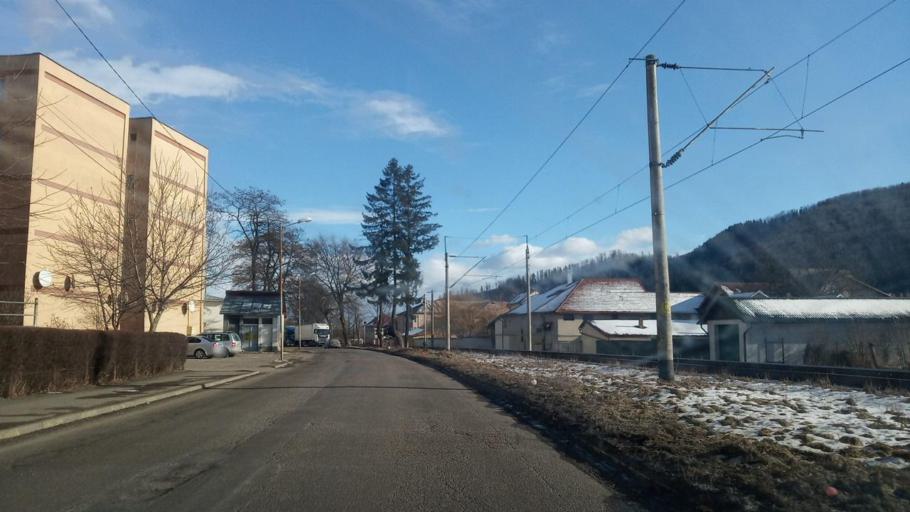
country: RO
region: Suceava
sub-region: Oras Gura Humorului
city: Gura Humorului
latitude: 47.5519
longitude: 25.8936
